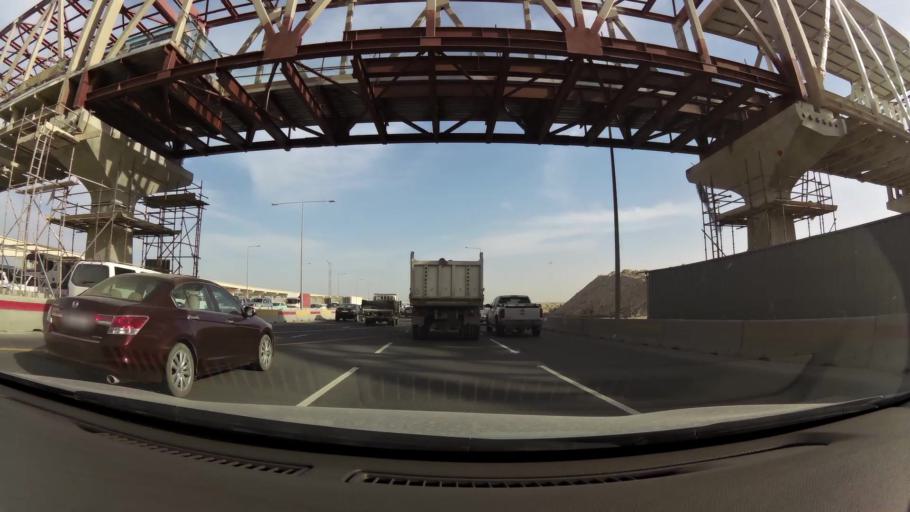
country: QA
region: Al Wakrah
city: Al Wakrah
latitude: 25.2108
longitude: 51.5851
